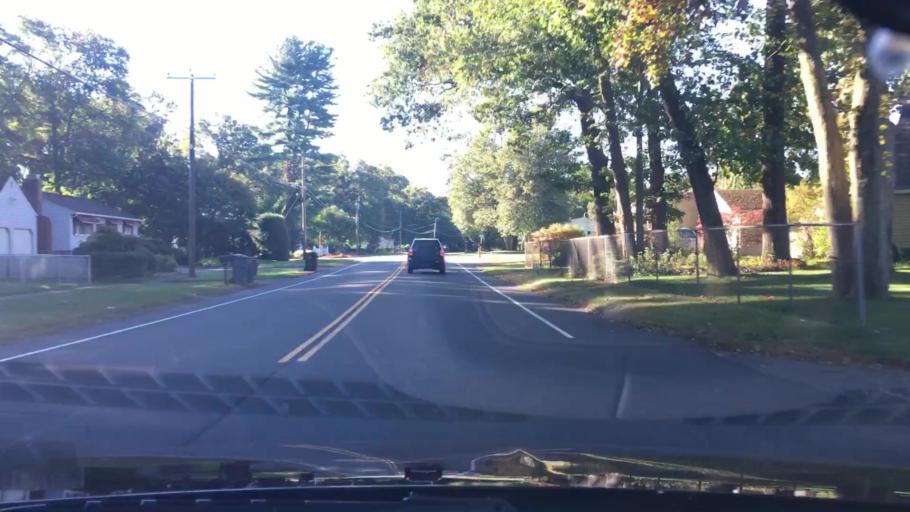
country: US
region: Connecticut
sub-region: Hartford County
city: Sherwood Manor
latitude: 42.0147
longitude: -72.5593
